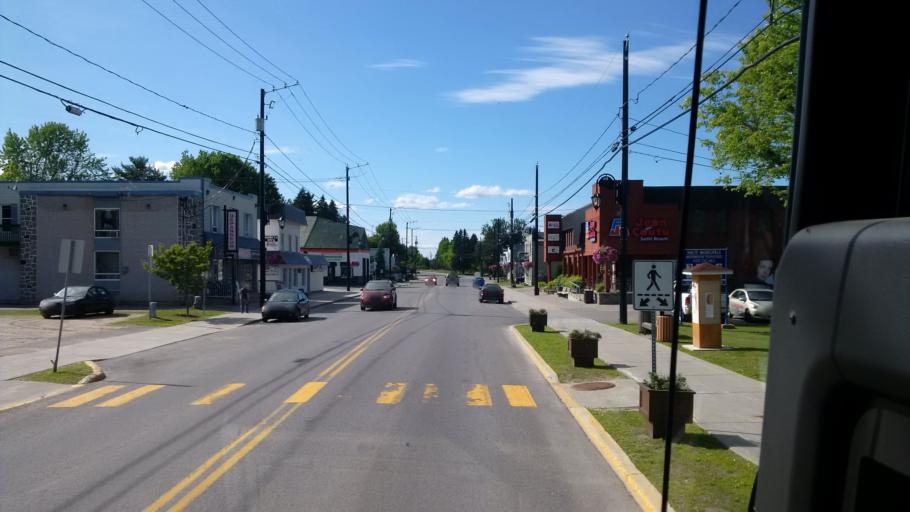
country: CA
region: Quebec
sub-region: Laurentides
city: Riviere-Rouge
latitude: 46.4150
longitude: -74.8720
